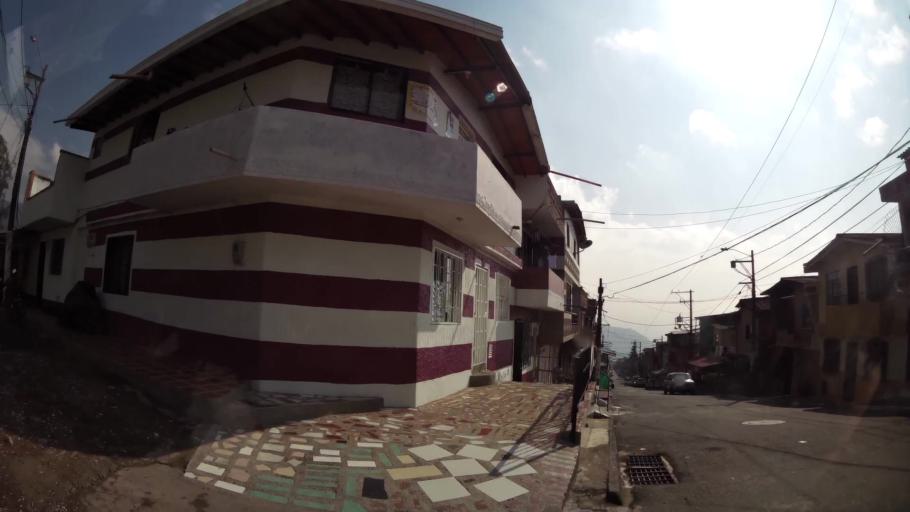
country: CO
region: Antioquia
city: La Estrella
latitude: 6.1704
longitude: -75.6433
